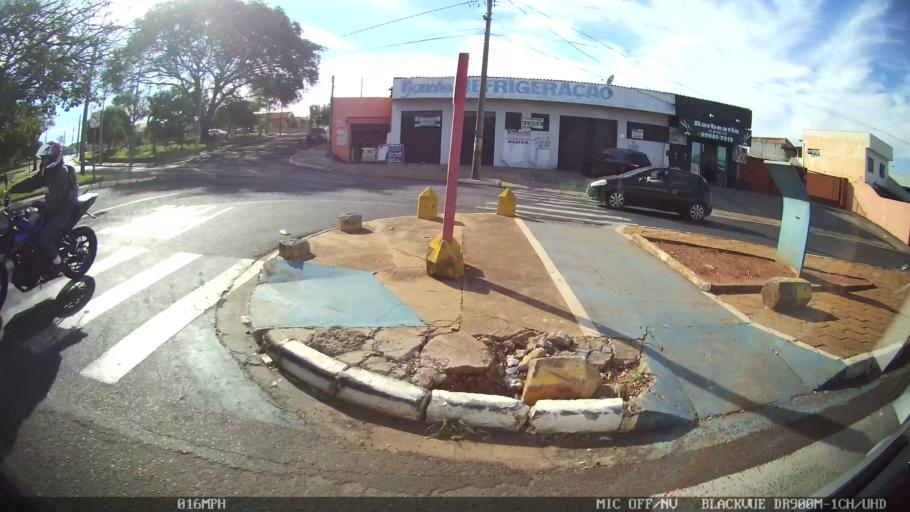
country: BR
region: Sao Paulo
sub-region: Araraquara
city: Araraquara
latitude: -21.7912
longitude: -48.1558
